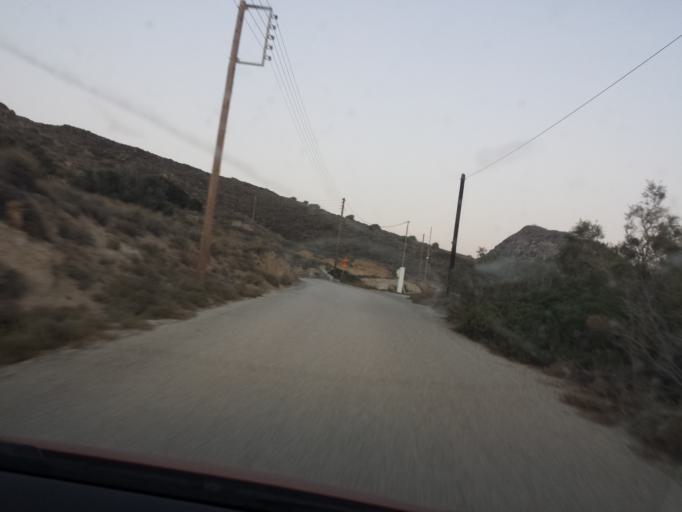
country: GR
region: South Aegean
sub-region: Nomos Kykladon
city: Milos
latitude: 36.7535
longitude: 24.4144
